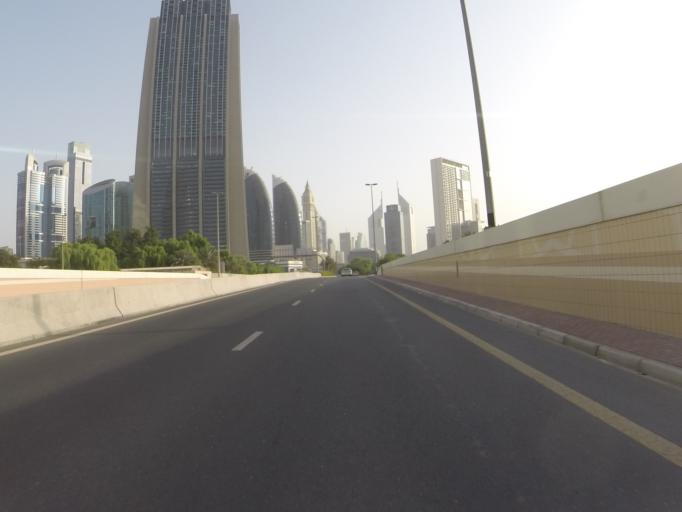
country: AE
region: Dubai
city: Dubai
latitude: 25.2034
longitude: 55.2786
